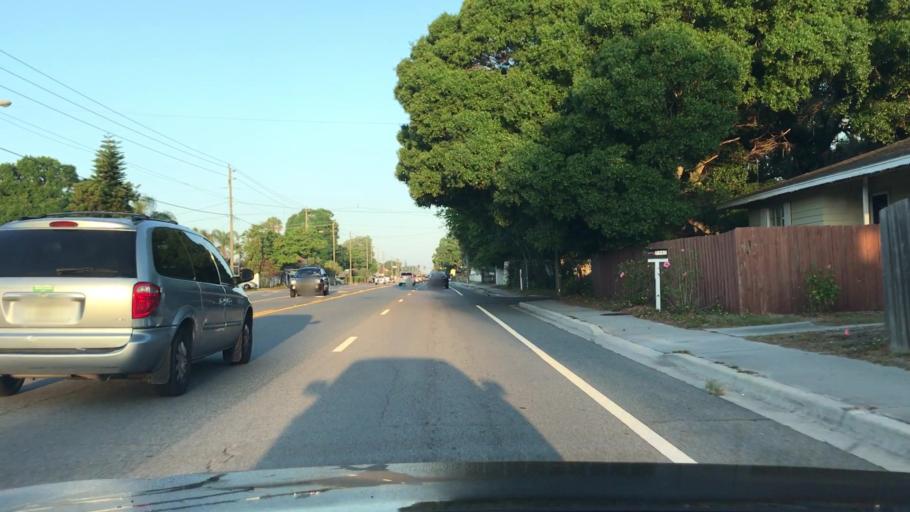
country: US
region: Florida
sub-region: Sarasota County
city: Southgate
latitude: 27.3229
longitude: -82.5104
